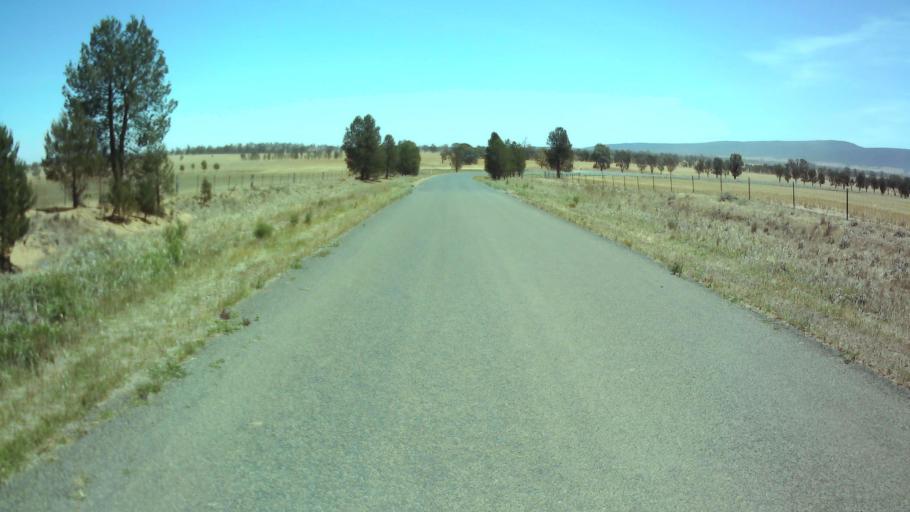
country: AU
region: New South Wales
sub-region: Weddin
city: Grenfell
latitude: -34.0498
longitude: 148.1759
